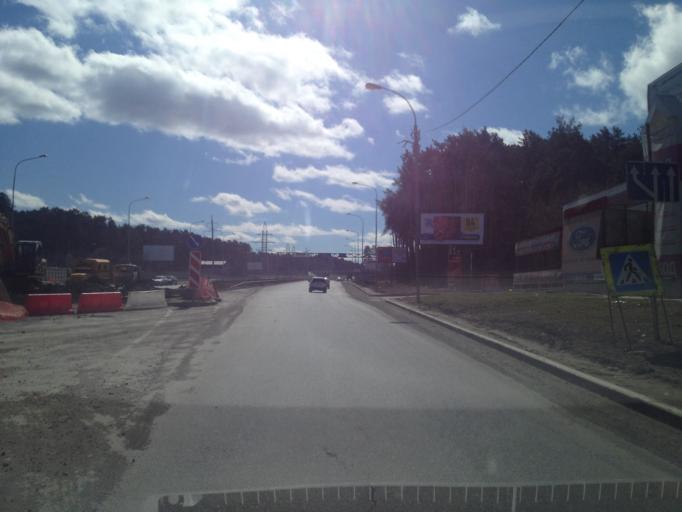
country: RU
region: Sverdlovsk
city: Sovkhoznyy
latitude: 56.7961
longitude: 60.5959
